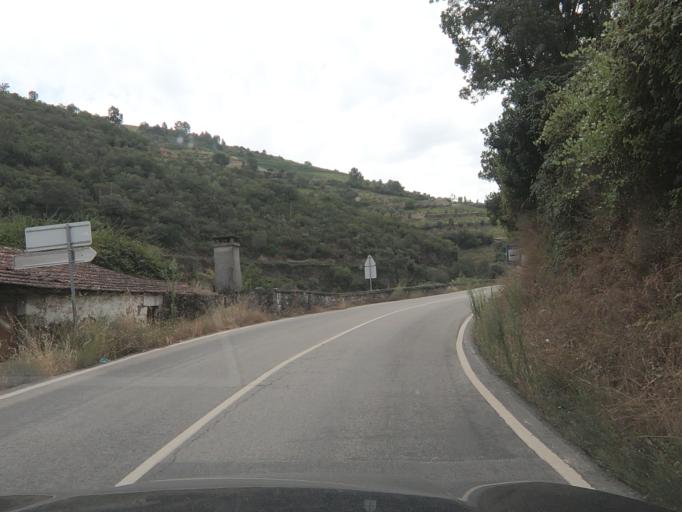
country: PT
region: Vila Real
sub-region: Santa Marta de Penaguiao
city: Santa Marta de Penaguiao
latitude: 41.2254
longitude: -7.7710
